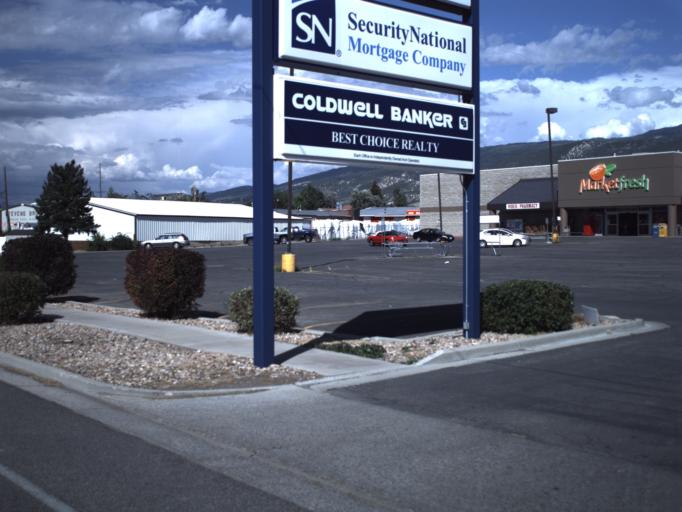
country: US
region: Utah
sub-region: Sanpete County
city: Ephraim
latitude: 39.3511
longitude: -111.5875
